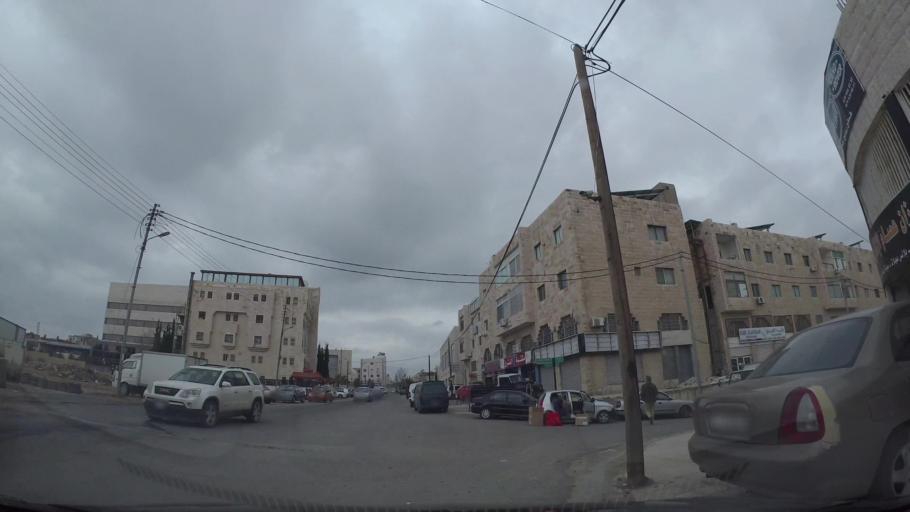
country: JO
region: Amman
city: Wadi as Sir
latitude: 31.9446
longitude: 35.8436
